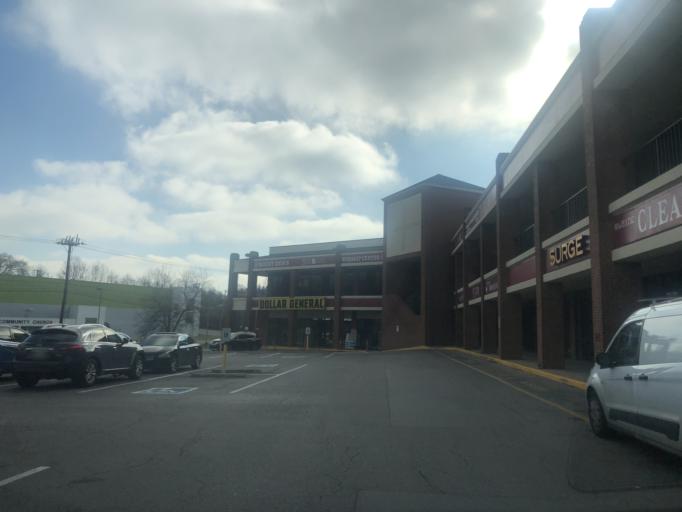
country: US
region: Tennessee
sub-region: Rutherford County
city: La Vergne
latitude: 36.0859
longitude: -86.6501
